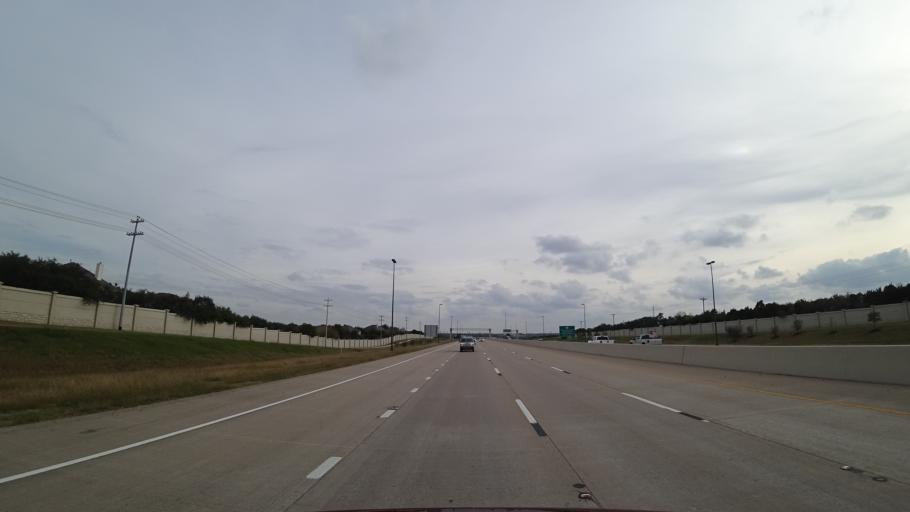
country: US
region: Texas
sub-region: Williamson County
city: Cedar Park
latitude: 30.5099
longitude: -97.8114
